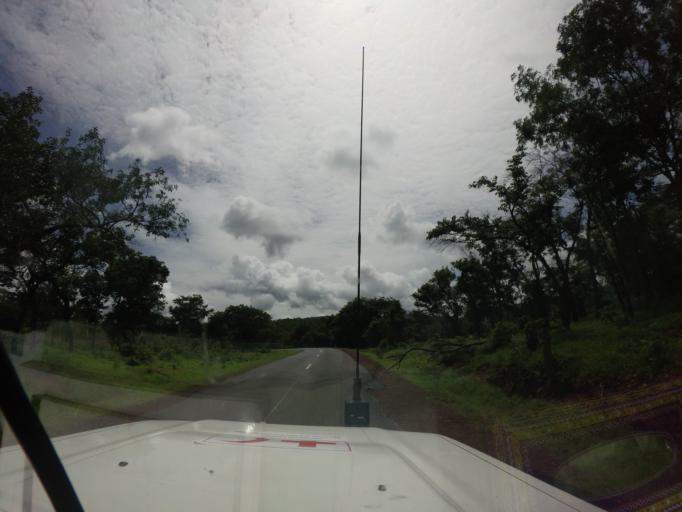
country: SL
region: Northern Province
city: Gberia Fotombu
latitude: 10.1758
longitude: -11.2016
